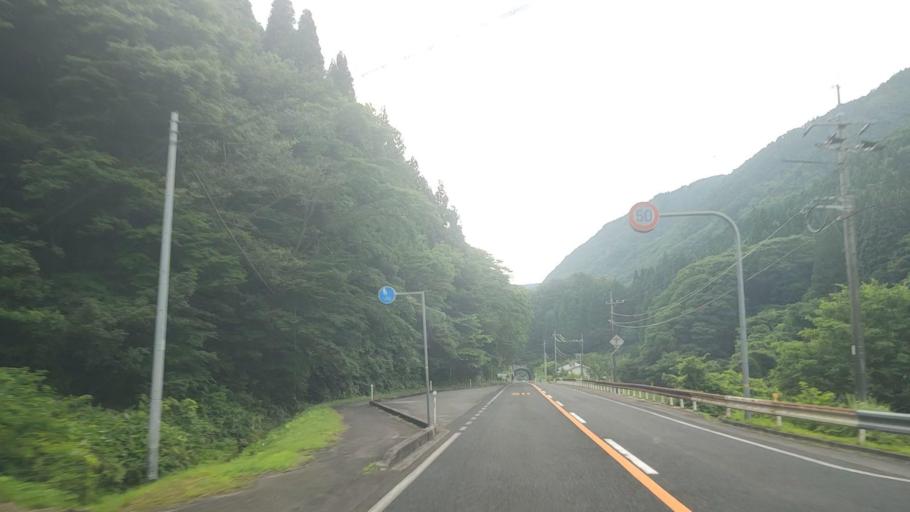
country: JP
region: Tottori
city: Kurayoshi
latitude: 35.3155
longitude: 133.8787
